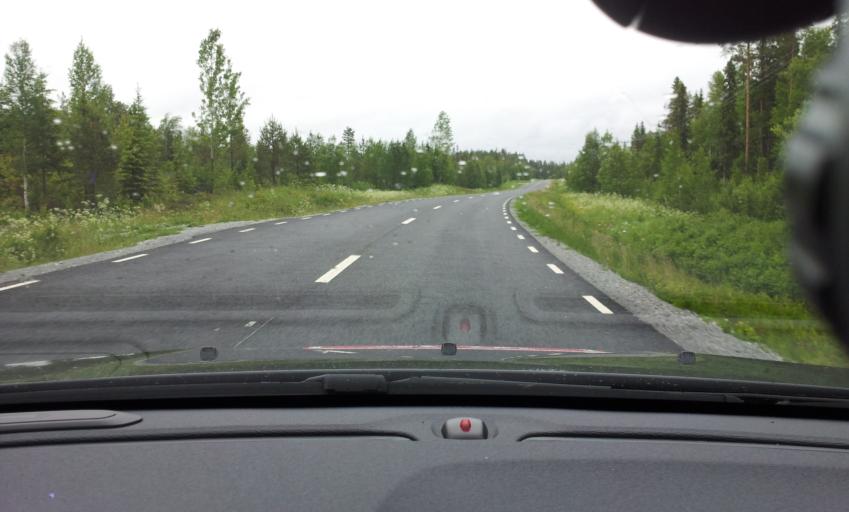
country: SE
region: Jaemtland
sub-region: OEstersunds Kommun
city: Lit
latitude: 63.7380
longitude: 14.7628
